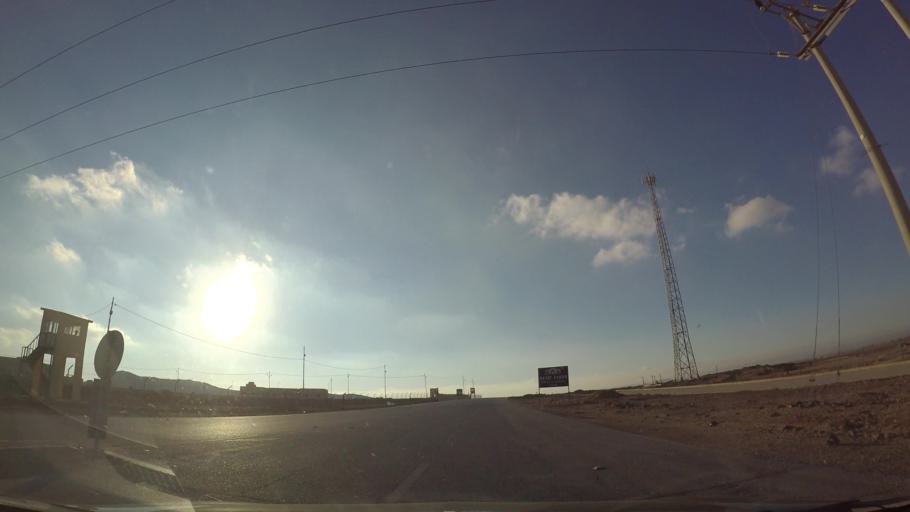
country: JO
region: Tafielah
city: Busayra
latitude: 30.4988
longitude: 35.7964
